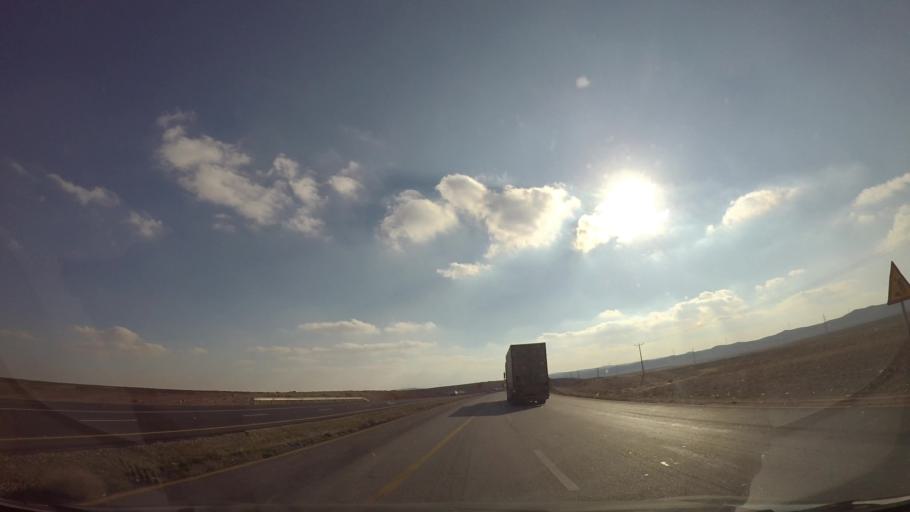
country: JO
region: Karak
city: Karak City
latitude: 31.1309
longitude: 36.0251
